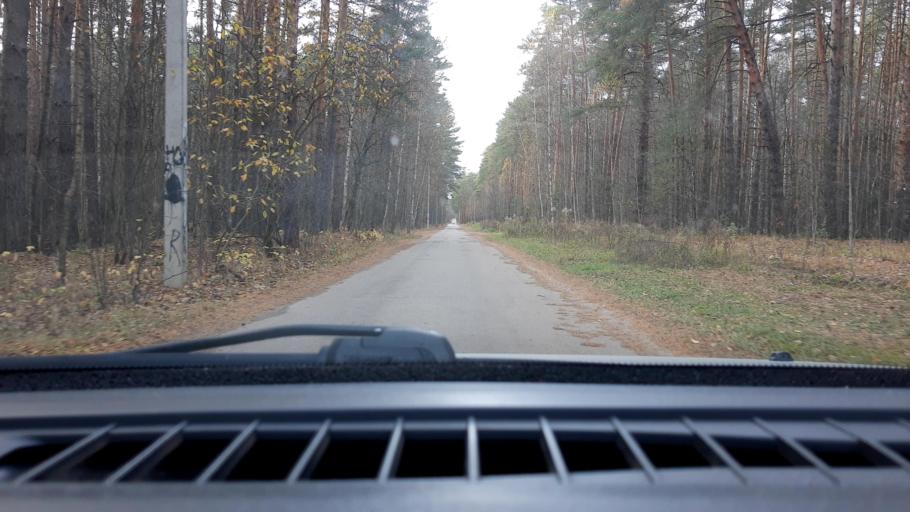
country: RU
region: Nizjnij Novgorod
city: Kstovo
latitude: 56.1678
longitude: 44.1146
